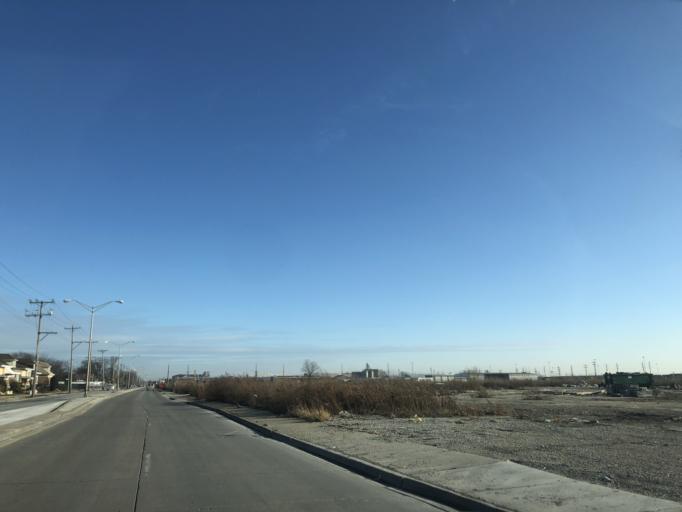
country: US
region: Illinois
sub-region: Cook County
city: Burbank
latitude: 41.7744
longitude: -87.7613
